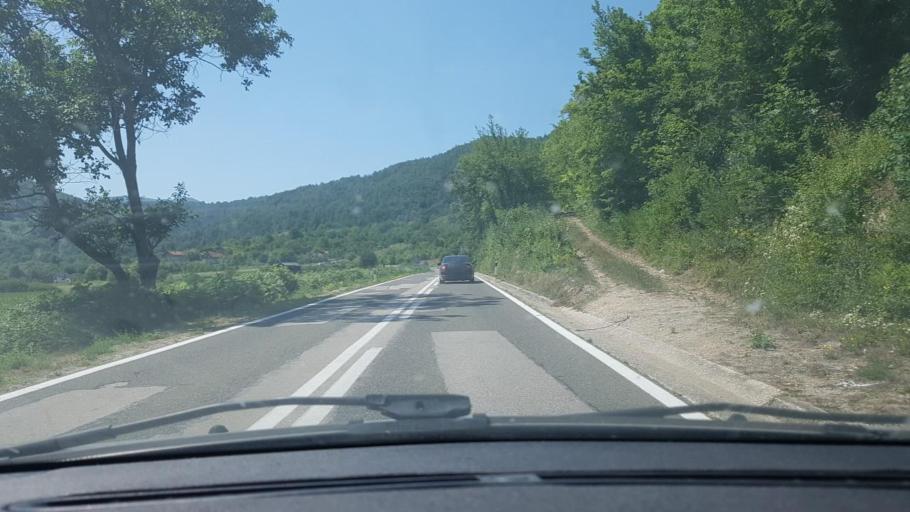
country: BA
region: Federation of Bosnia and Herzegovina
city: Bihac
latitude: 44.7512
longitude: 15.9357
